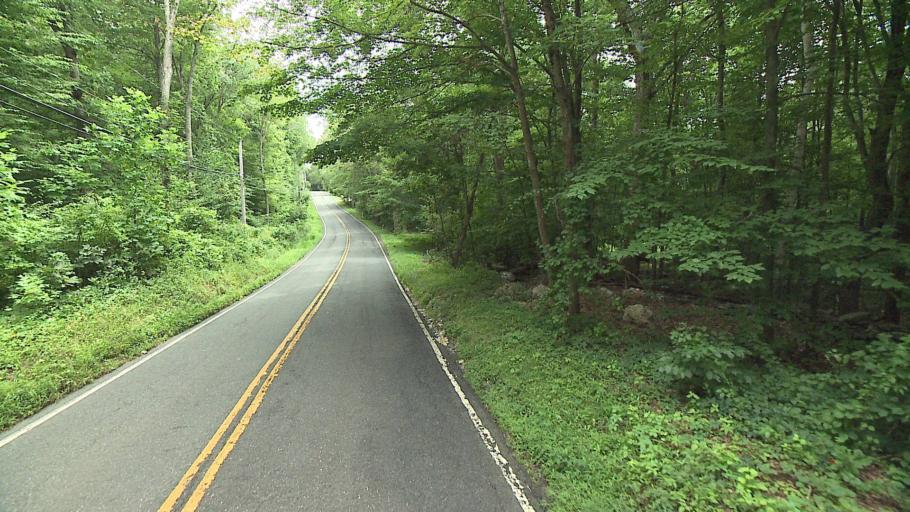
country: US
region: Connecticut
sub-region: Litchfield County
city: Woodbury
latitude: 41.5503
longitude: -73.2445
